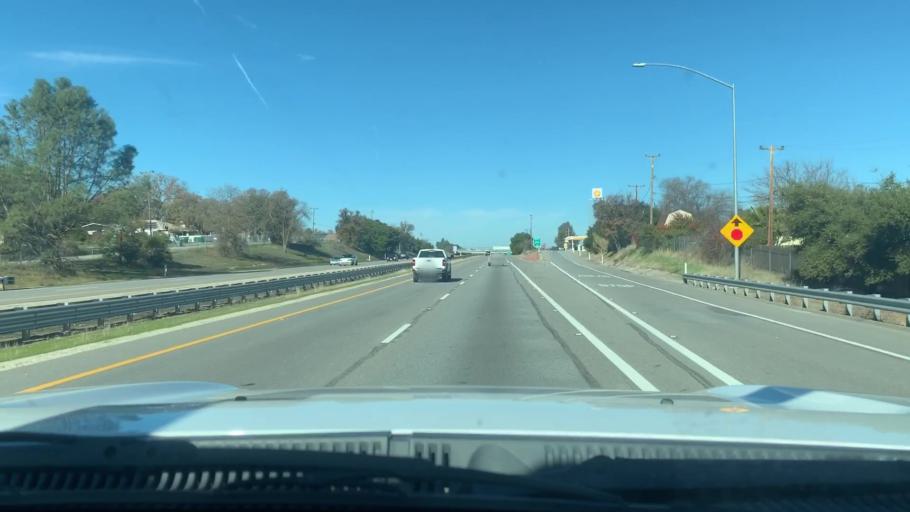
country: US
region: California
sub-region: San Luis Obispo County
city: Atascadero
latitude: 35.4609
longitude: -120.6472
